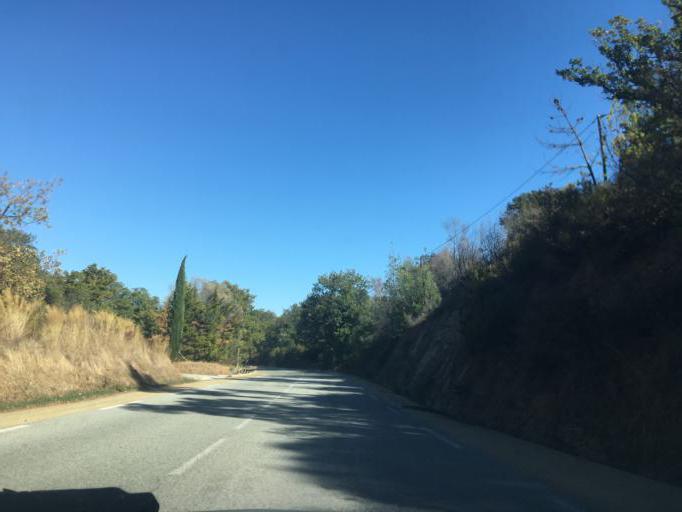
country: FR
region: Provence-Alpes-Cote d'Azur
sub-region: Departement du Var
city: La Garde-Freinet
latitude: 43.2999
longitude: 6.4799
